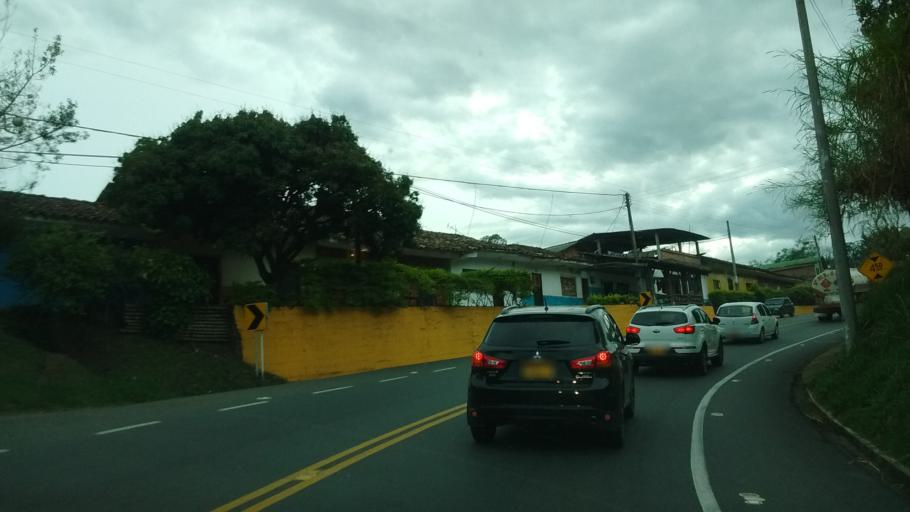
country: CO
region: Cauca
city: Caldono
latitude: 2.7996
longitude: -76.5531
